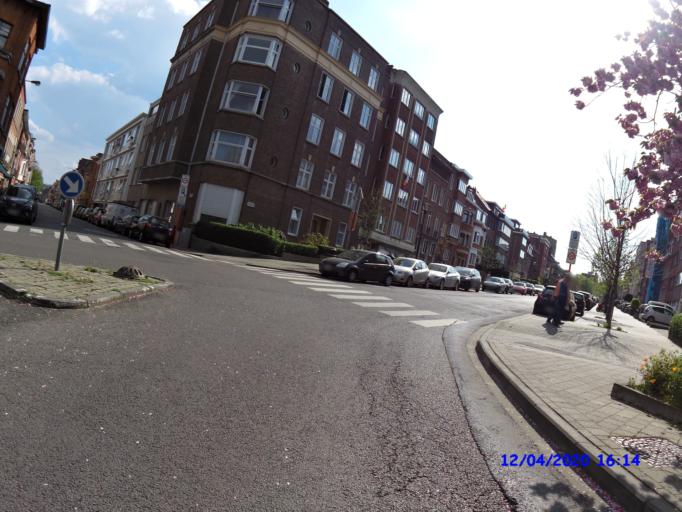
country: BE
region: Flanders
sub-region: Provincie Vlaams-Brabant
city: Diegem
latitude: 50.8478
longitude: 4.4081
